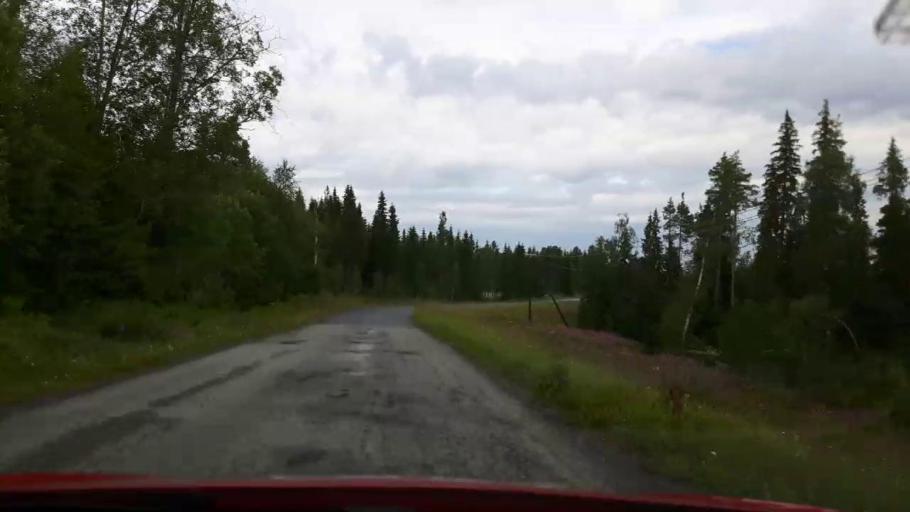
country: SE
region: Jaemtland
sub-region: Stroemsunds Kommun
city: Stroemsund
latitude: 63.5317
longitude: 15.3549
